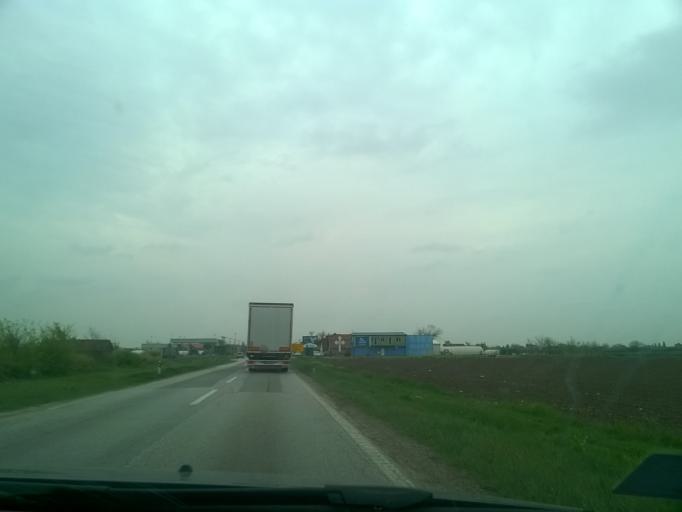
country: RS
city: Hrtkovci
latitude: 44.8929
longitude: 19.7640
